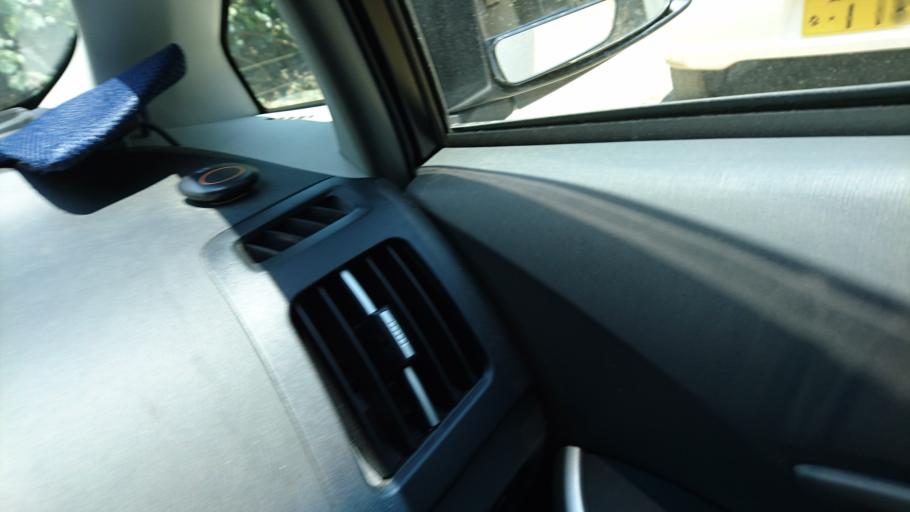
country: JP
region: Ehime
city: Ozu
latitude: 33.5108
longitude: 132.5316
